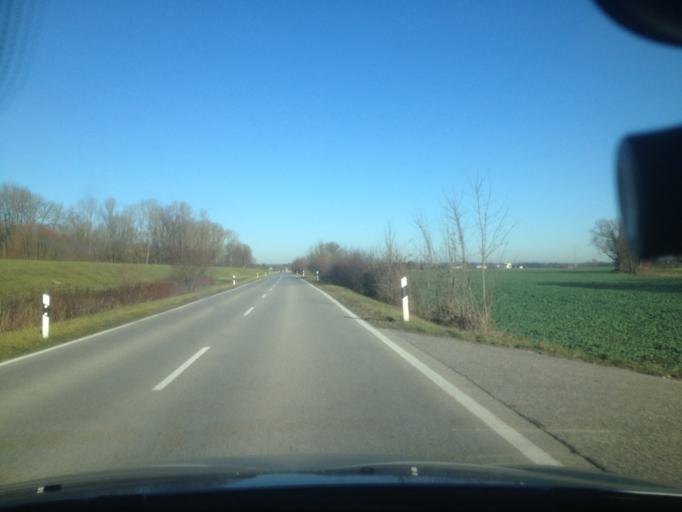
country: DE
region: Bavaria
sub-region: Upper Bavaria
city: Moosburg
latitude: 48.4487
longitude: 11.9461
